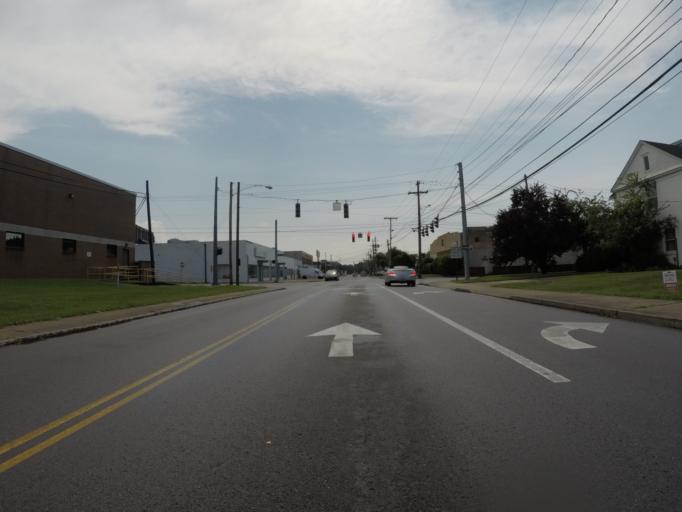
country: US
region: Kentucky
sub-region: Boyd County
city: Ashland
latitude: 38.4793
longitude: -82.6460
